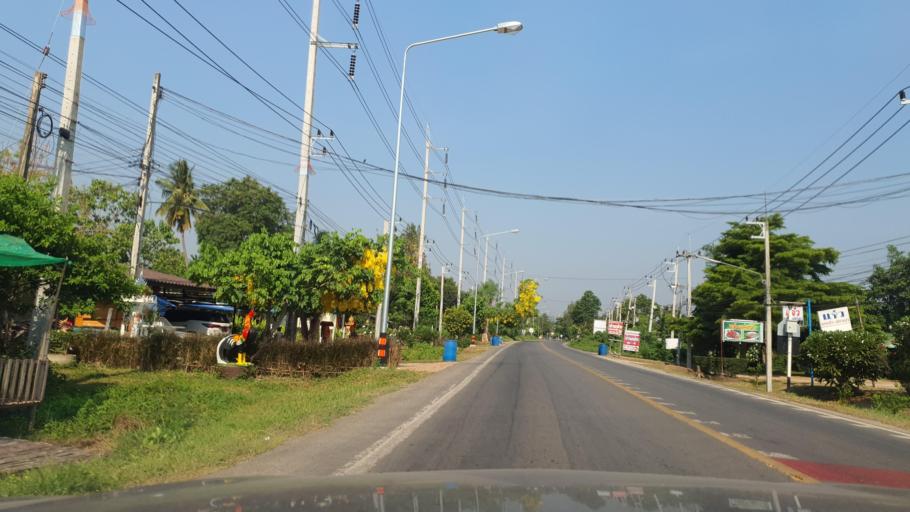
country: TH
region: Kanchanaburi
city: Kanchanaburi
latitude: 14.0359
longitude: 99.4924
